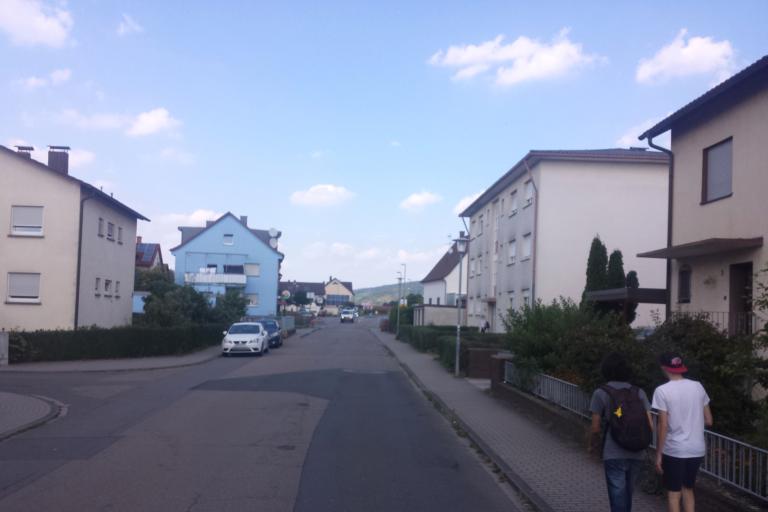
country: DE
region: Baden-Wuerttemberg
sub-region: Karlsruhe Region
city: Hemsbach
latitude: 49.5904
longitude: 8.6456
